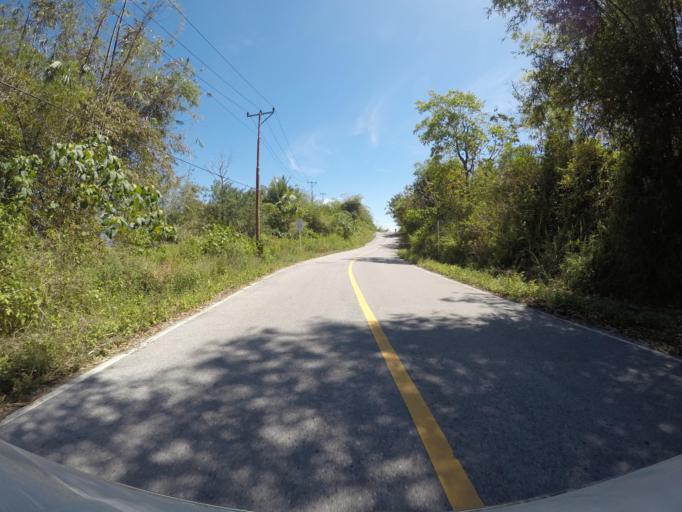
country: TL
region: Manatuto
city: Manatuto
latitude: -8.8749
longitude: 125.9931
